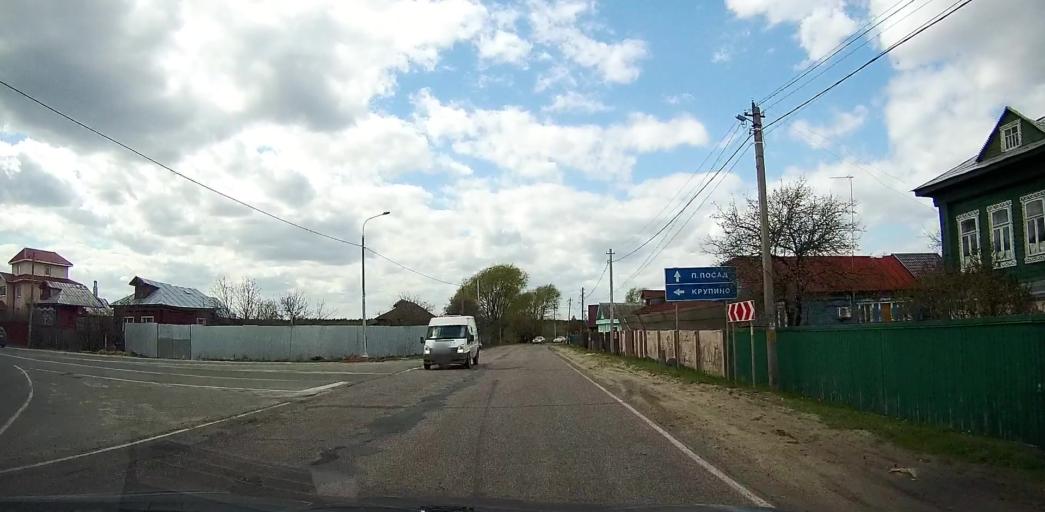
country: RU
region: Moskovskaya
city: Drezna
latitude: 55.6715
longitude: 38.7678
